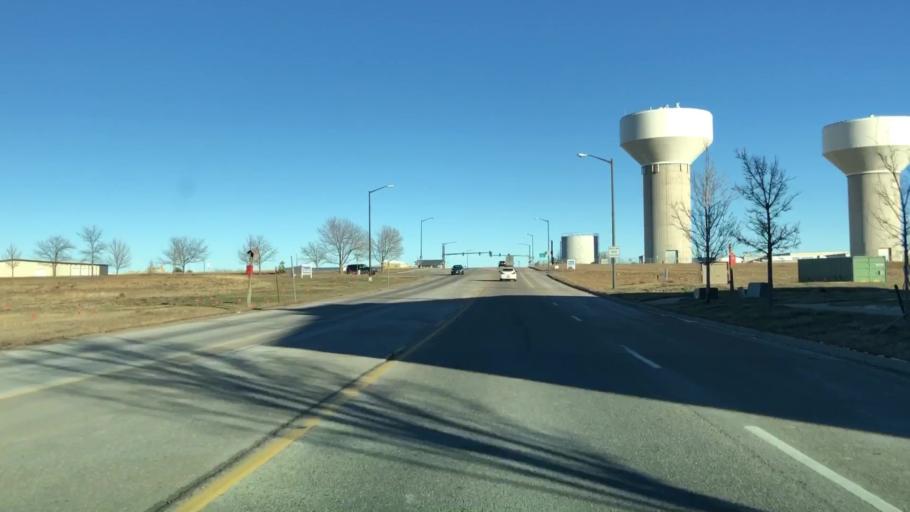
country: US
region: Colorado
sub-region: Weld County
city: Windsor
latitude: 40.4359
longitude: -104.9772
